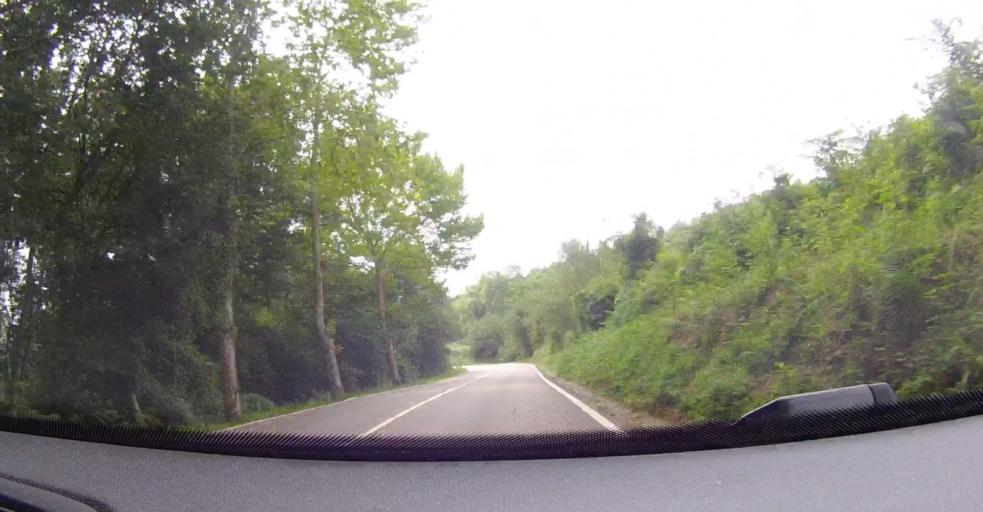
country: ES
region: Basque Country
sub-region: Bizkaia
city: Balmaseda
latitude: 43.2366
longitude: -3.2916
